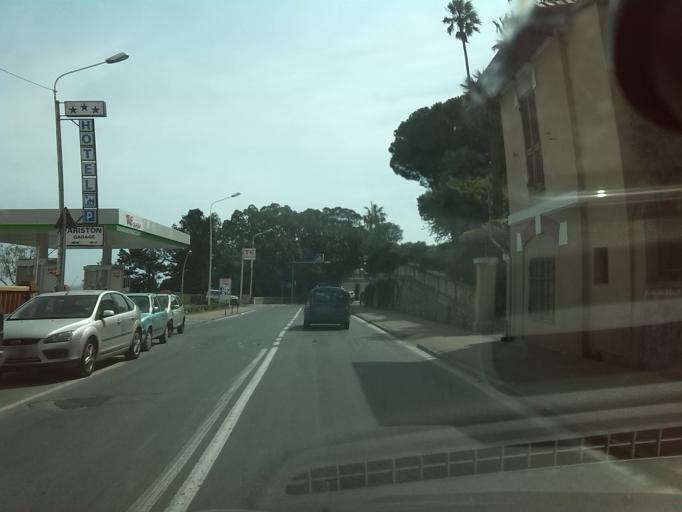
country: IT
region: Liguria
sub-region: Provincia di Imperia
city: Imperia
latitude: 43.8758
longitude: 8.0175
